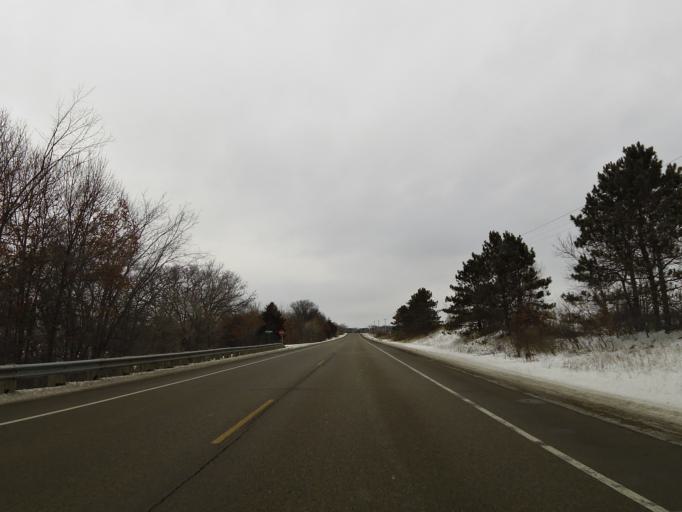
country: US
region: Wisconsin
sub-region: Saint Croix County
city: North Hudson
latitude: 45.0209
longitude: -92.7452
